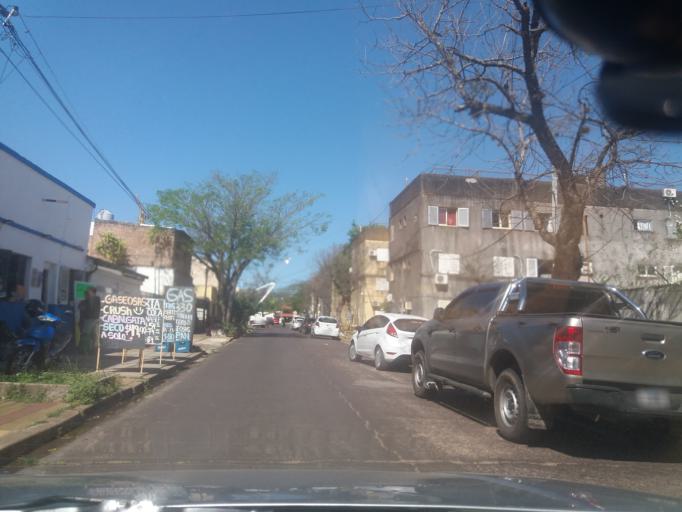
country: AR
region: Corrientes
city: Corrientes
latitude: -27.4726
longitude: -58.8472
